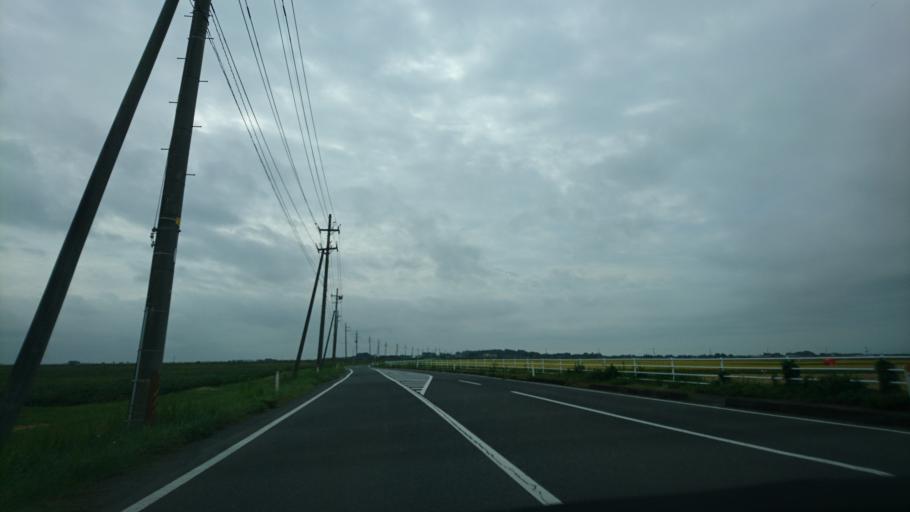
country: JP
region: Iwate
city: Ichinoseki
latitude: 38.7990
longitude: 141.1217
